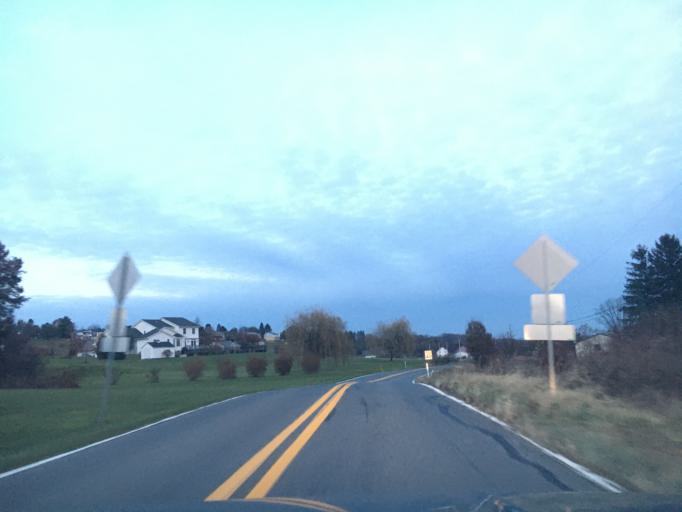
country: US
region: Pennsylvania
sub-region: Lehigh County
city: Schnecksville
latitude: 40.6989
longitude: -75.5817
